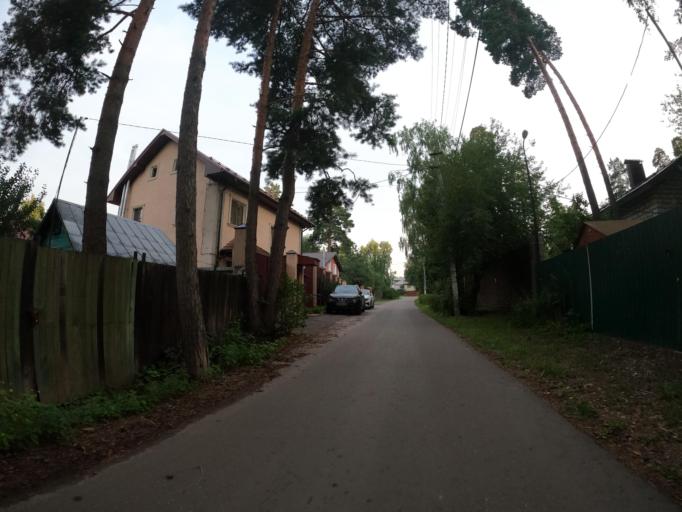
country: RU
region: Moskovskaya
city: Bykovo
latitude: 55.6402
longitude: 38.0818
